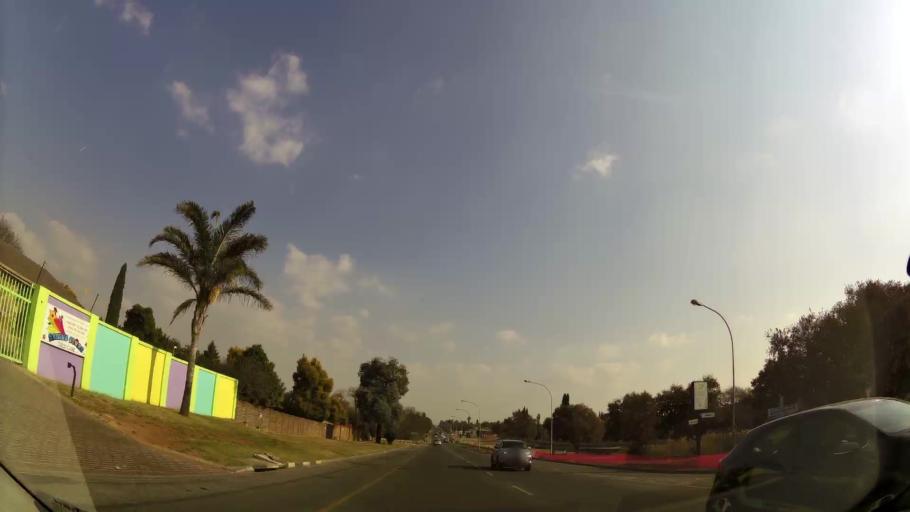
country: ZA
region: Gauteng
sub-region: Ekurhuleni Metropolitan Municipality
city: Benoni
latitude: -26.1585
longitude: 28.2883
